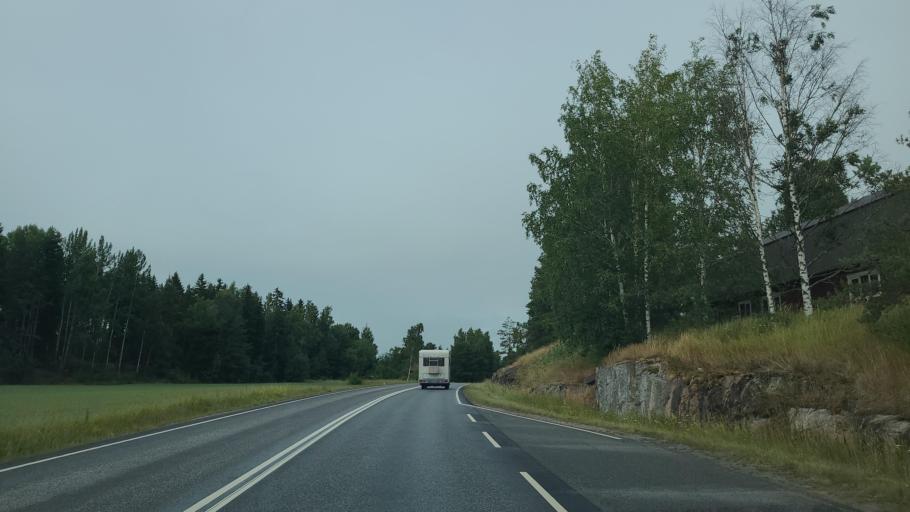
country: FI
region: Varsinais-Suomi
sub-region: Turku
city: Sauvo
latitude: 60.2908
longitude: 22.6726
